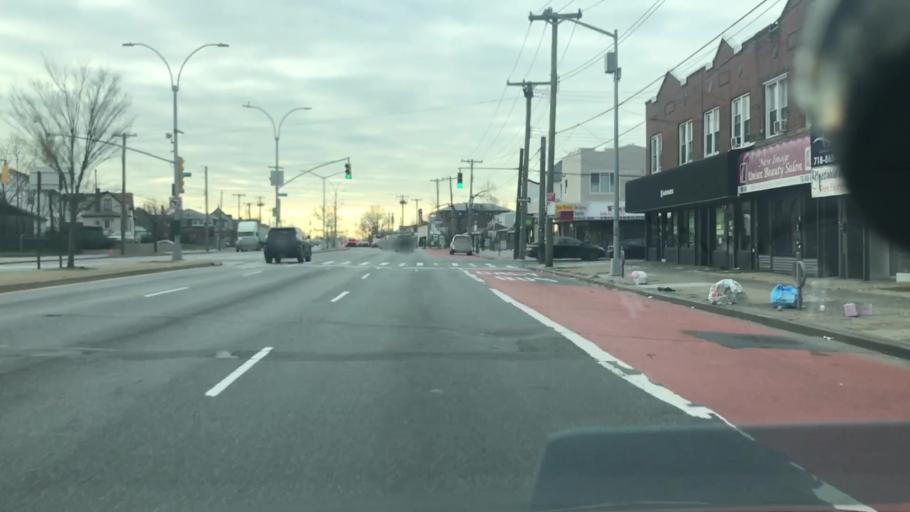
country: US
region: New York
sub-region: Queens County
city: Borough of Queens
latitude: 40.6792
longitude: -73.8445
